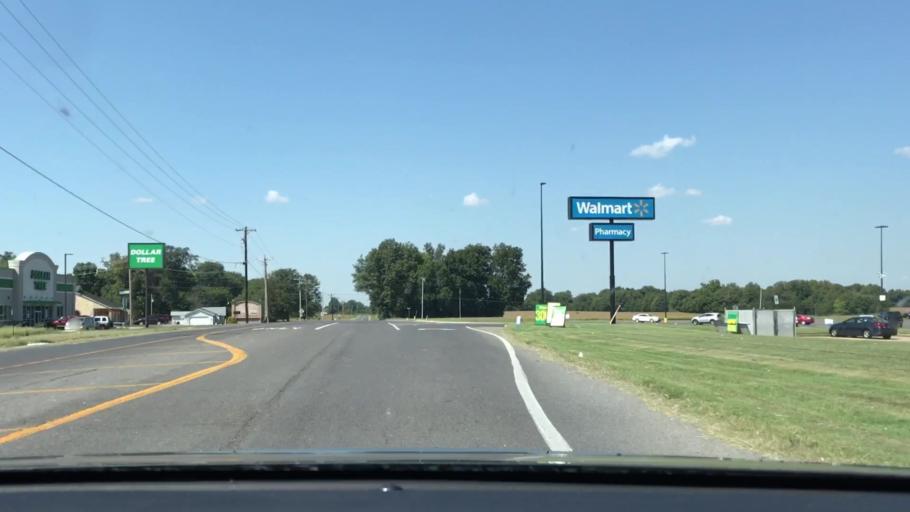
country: US
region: Kentucky
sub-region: Fulton County
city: Fulton
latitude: 36.5155
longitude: -88.8995
